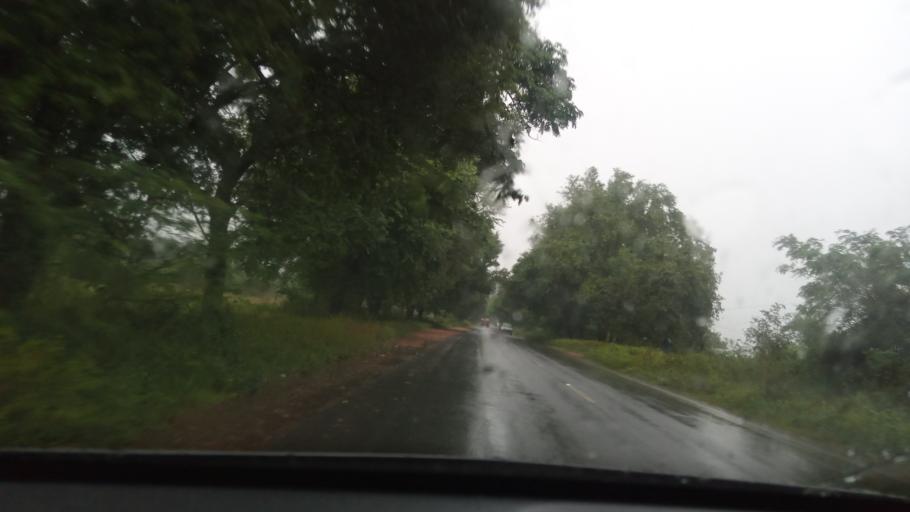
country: IN
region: Tamil Nadu
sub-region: Vellore
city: Kalavai
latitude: 12.8095
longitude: 79.4133
